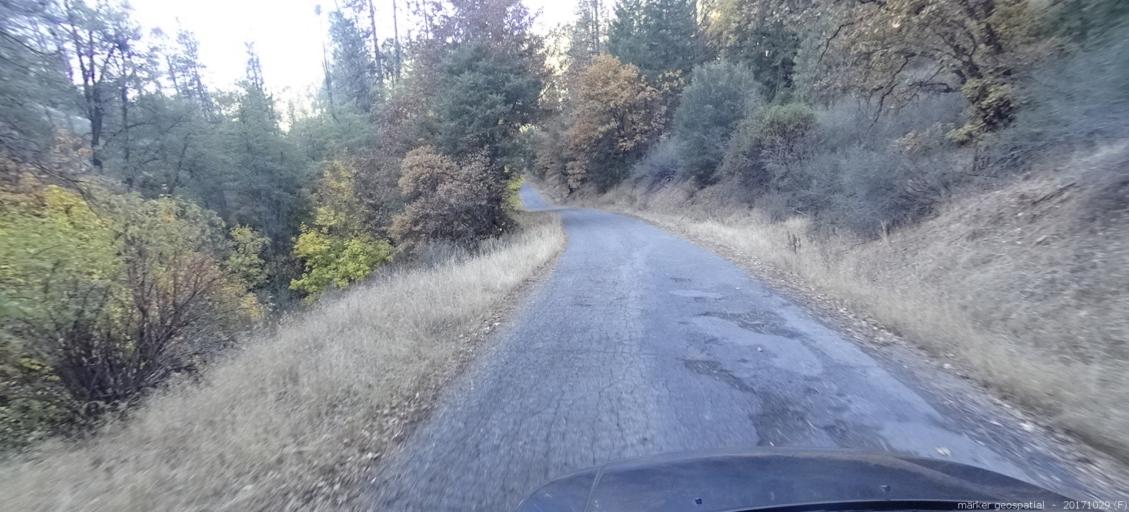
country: US
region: California
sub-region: Trinity County
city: Hayfork
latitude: 40.3929
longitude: -122.9845
